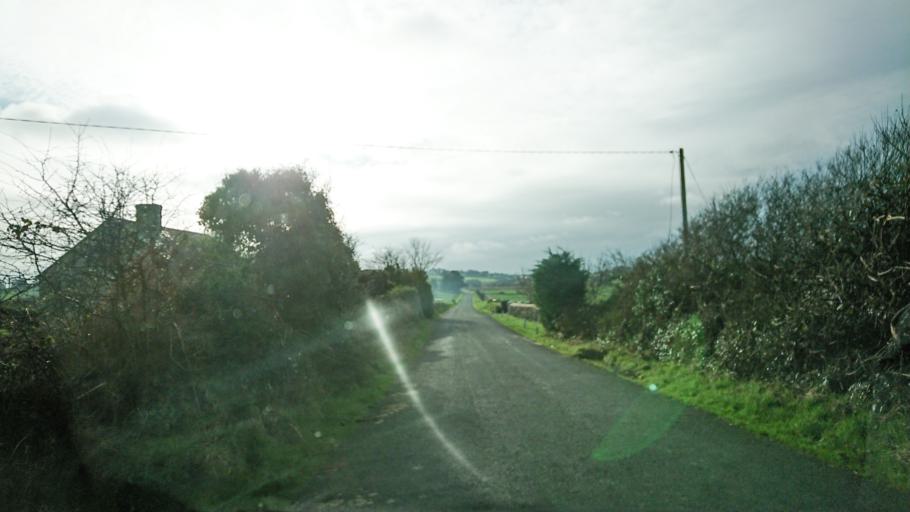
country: IE
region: Munster
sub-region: Waterford
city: Tra Mhor
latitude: 52.1655
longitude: -7.1871
